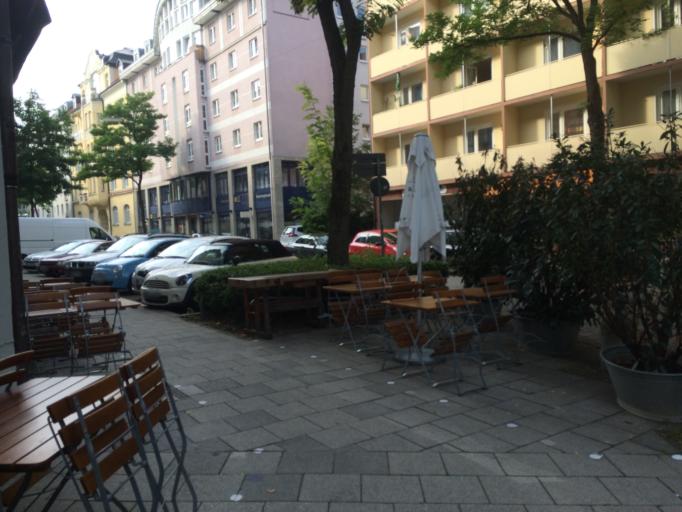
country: DE
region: Bavaria
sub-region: Upper Bavaria
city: Munich
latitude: 48.1634
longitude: 11.5843
